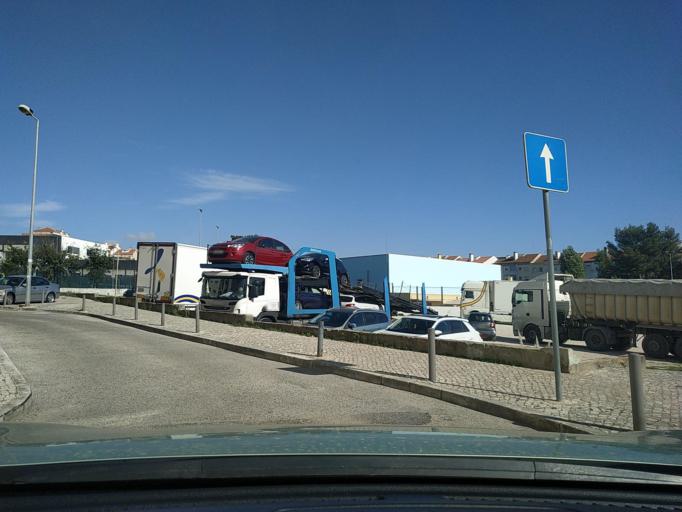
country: PT
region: Lisbon
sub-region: Sintra
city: Queluz
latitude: 38.7589
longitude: -9.2487
